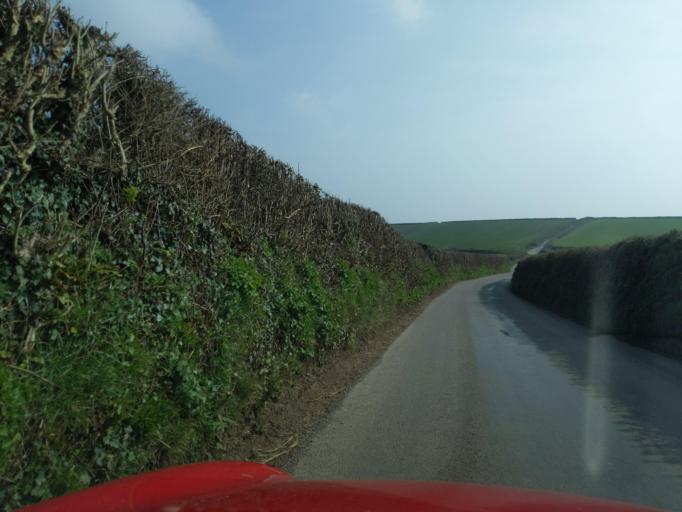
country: GB
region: England
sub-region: Devon
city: Salcombe
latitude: 50.2606
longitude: -3.7156
